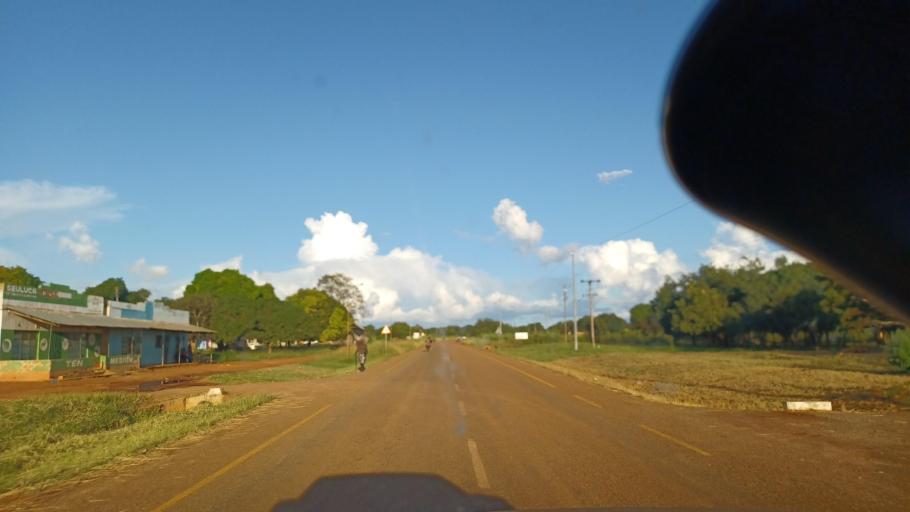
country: ZM
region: North-Western
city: Kalengwa
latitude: -13.1383
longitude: 25.0131
